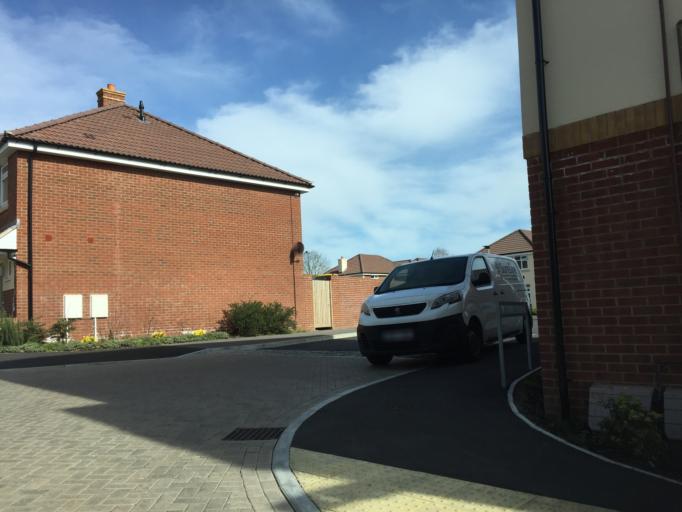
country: GB
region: England
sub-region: Wiltshire
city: Chippenham
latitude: 51.4631
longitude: -2.1327
